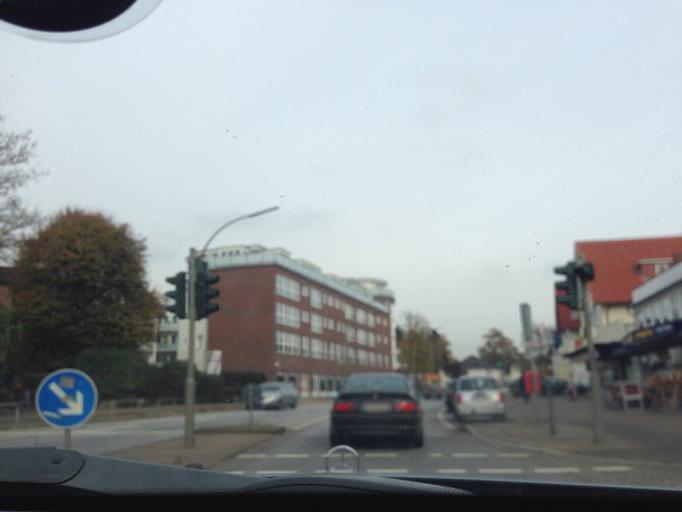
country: DE
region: Schleswig-Holstein
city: Barsbuettel
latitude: 53.6040
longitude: 10.1600
